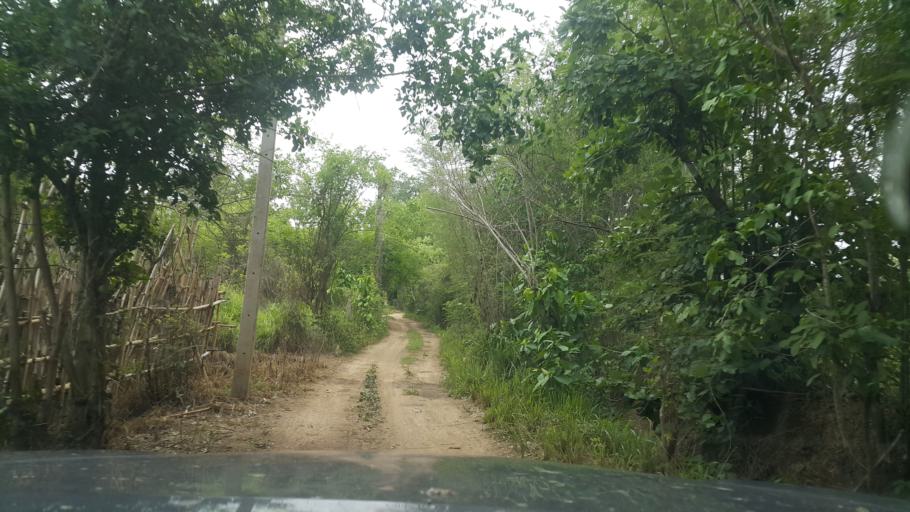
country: TH
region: Chiang Mai
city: Hang Dong
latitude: 18.6810
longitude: 98.8928
